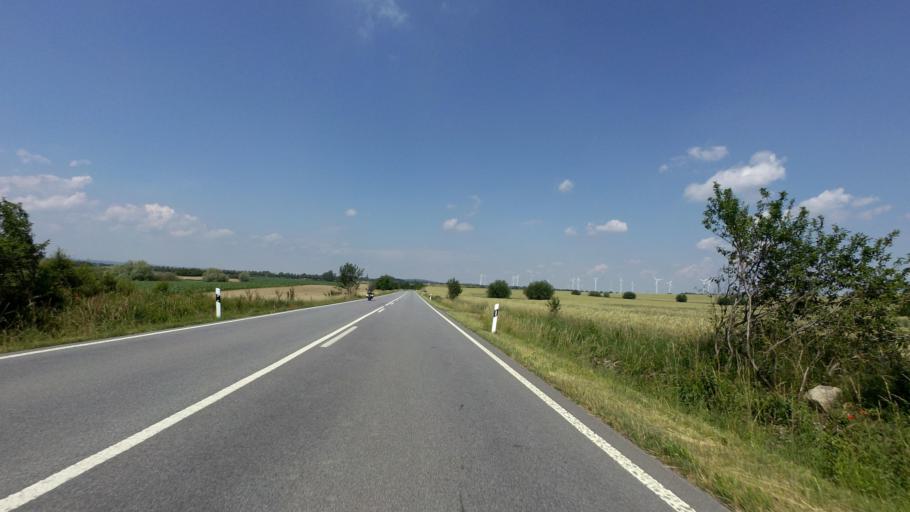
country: DE
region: Brandenburg
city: Oderberg
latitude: 52.9197
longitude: 14.0437
